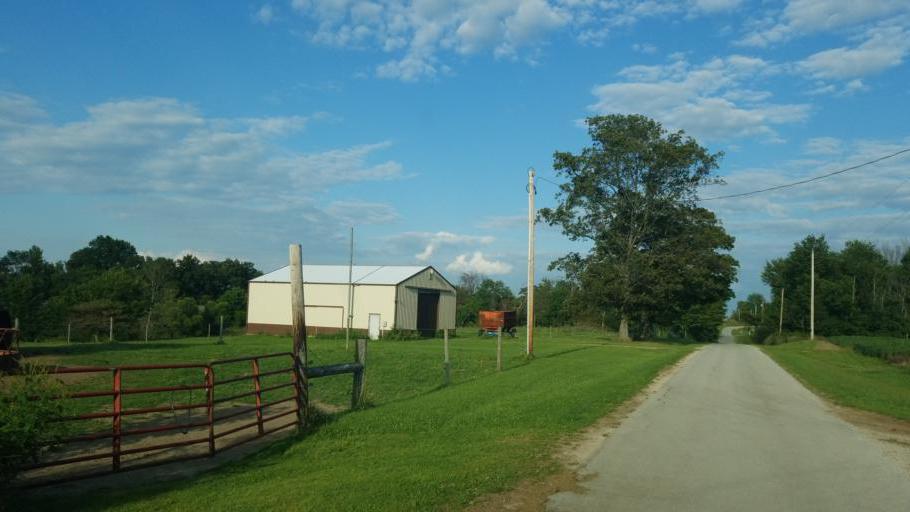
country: US
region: Ohio
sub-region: Sandusky County
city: Green Springs
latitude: 41.1102
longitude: -83.0030
